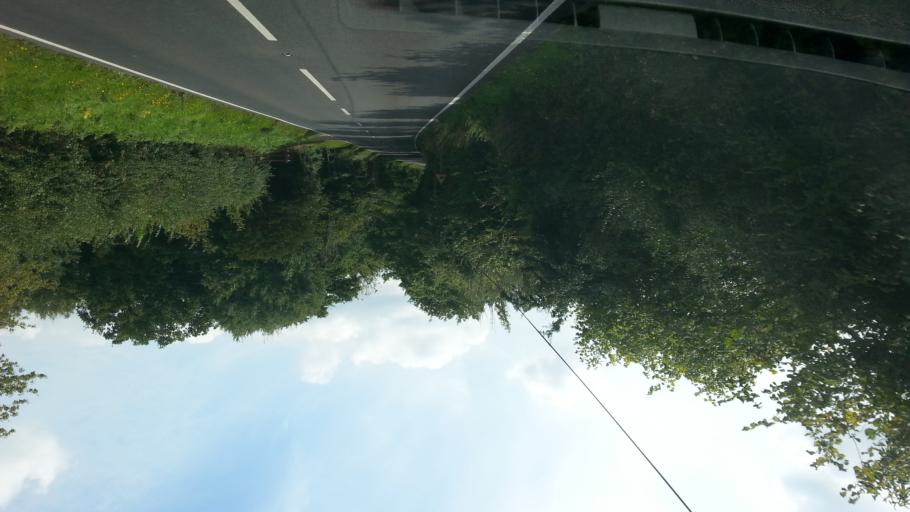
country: GB
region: England
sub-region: Surrey
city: Ottershaw
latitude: 51.3558
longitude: -0.5555
